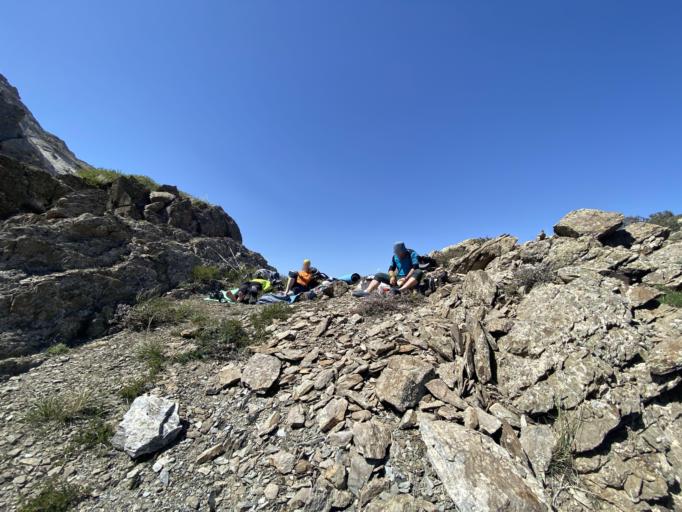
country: KZ
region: Ongtustik Qazaqstan
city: Kentau
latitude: 43.9606
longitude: 68.2471
